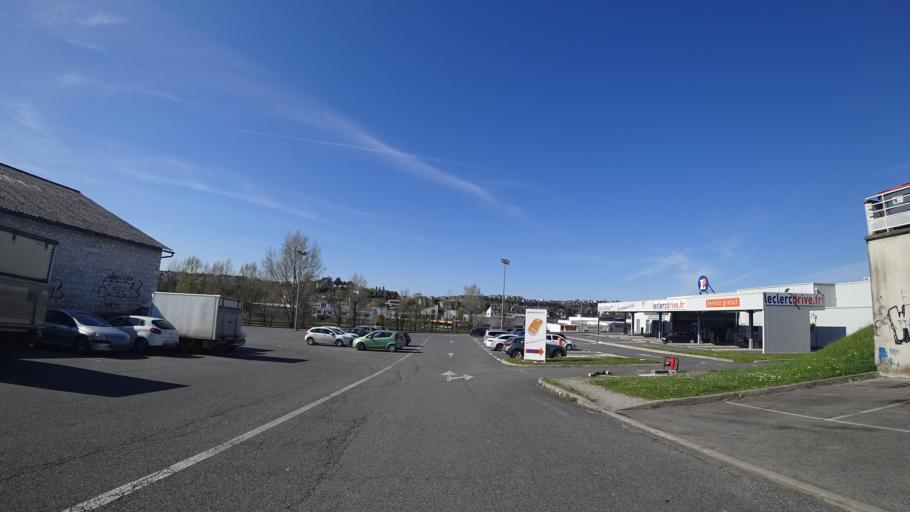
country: FR
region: Midi-Pyrenees
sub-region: Departement de l'Aveyron
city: Rodez
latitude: 44.3622
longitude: 2.5728
